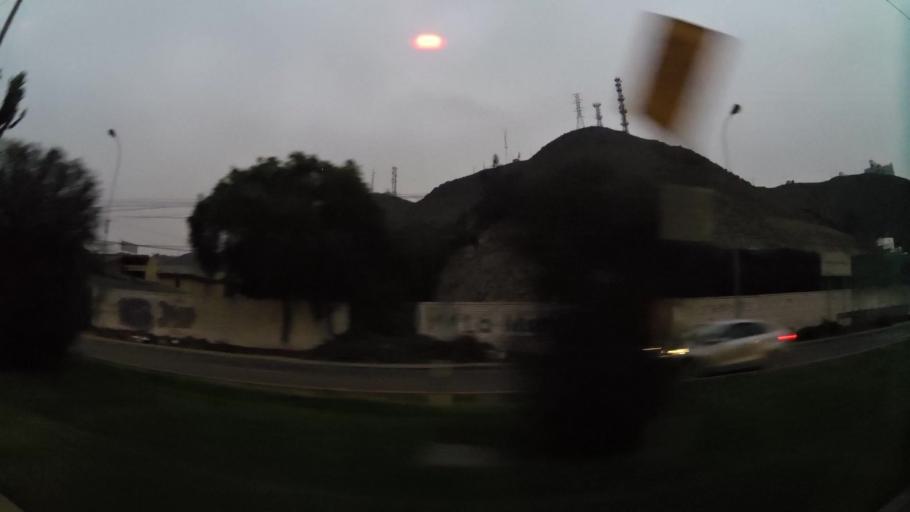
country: PE
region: Lima
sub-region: Lima
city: La Molina
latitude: -12.0853
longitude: -76.9575
